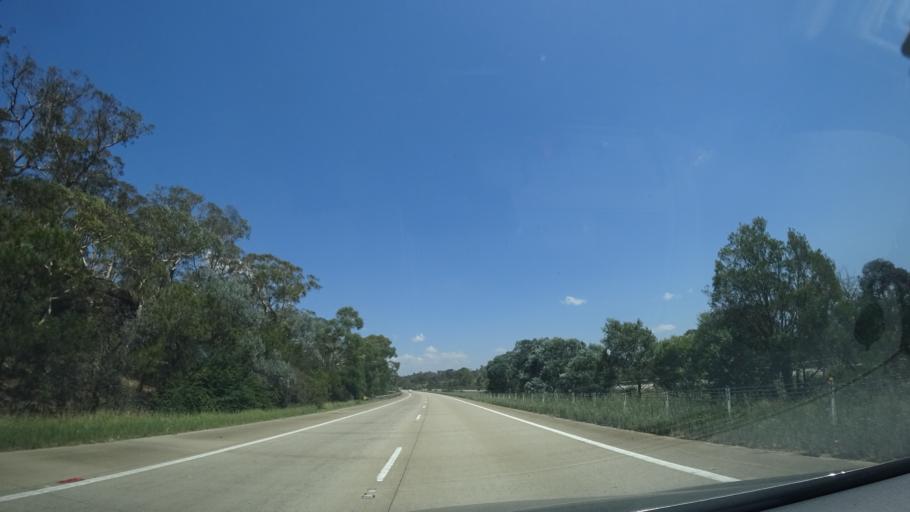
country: AU
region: New South Wales
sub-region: Wingecarribee
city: Moss Vale
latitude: -34.4825
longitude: 150.3141
